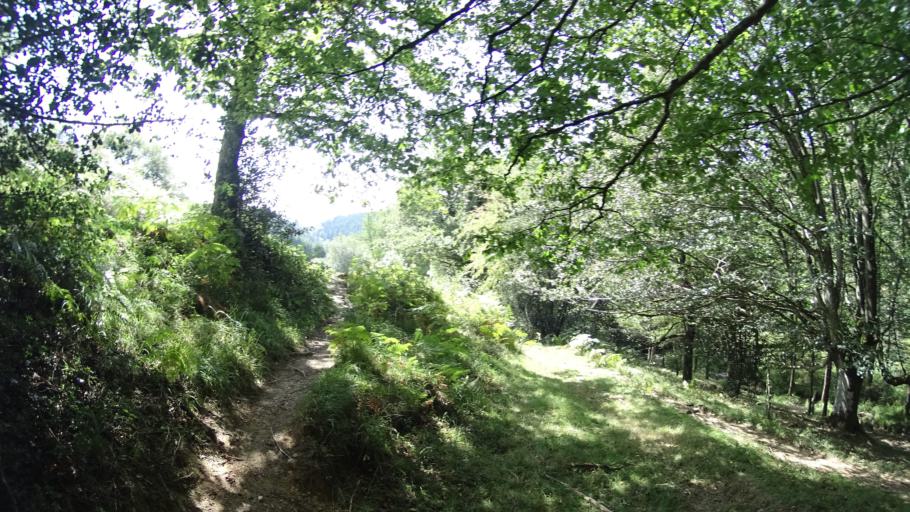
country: ES
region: Basque Country
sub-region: Bizkaia
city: Zeanuri
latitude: 43.0481
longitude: -2.7126
